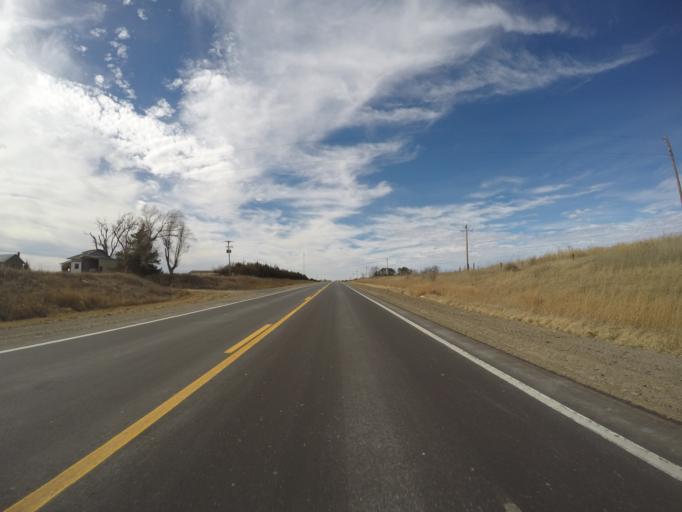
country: US
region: Nebraska
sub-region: Franklin County
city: Franklin
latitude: 40.0962
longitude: -98.9280
